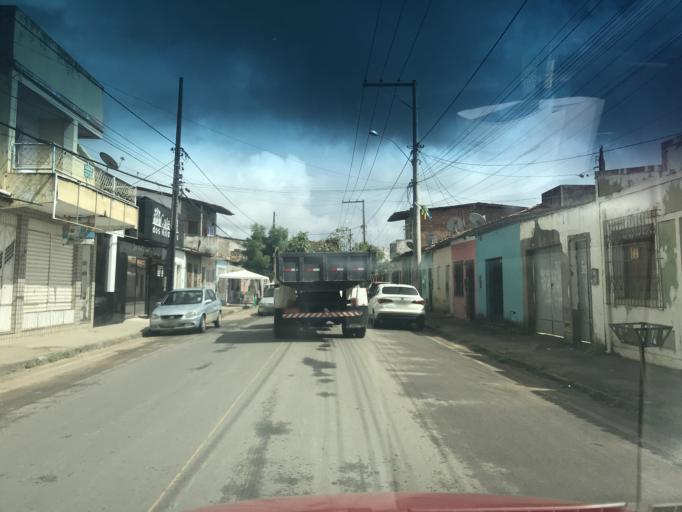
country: BR
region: Bahia
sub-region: Cruz Das Almas
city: Cruz das Almas
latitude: -12.6789
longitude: -39.0965
